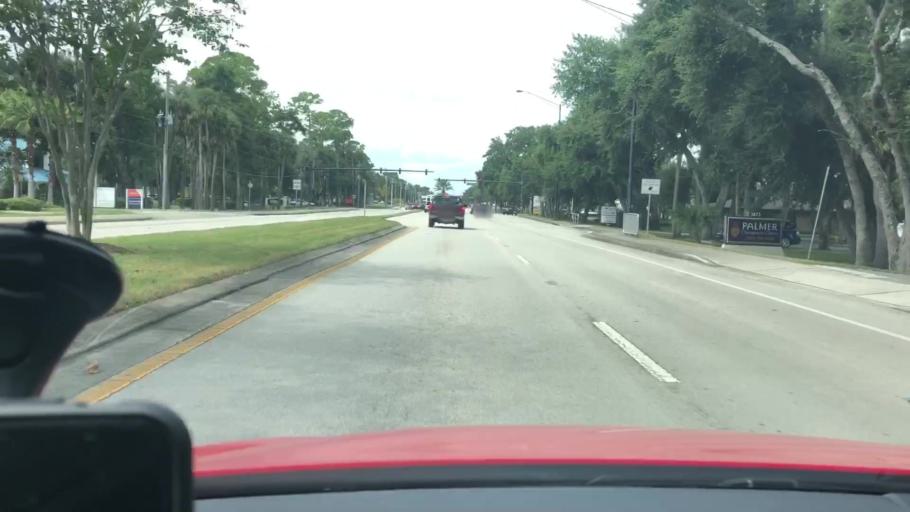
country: US
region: Florida
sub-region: Volusia County
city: Port Orange
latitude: 29.1234
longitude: -81.0027
